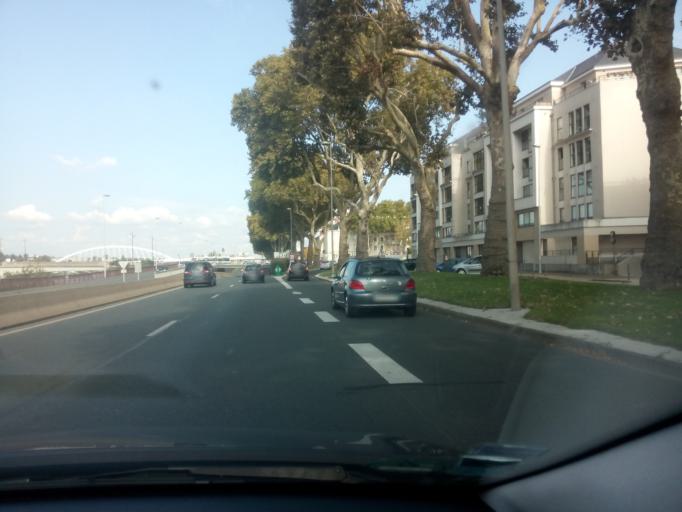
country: FR
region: Pays de la Loire
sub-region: Departement de Maine-et-Loire
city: Angers
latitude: 47.4757
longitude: -0.5546
